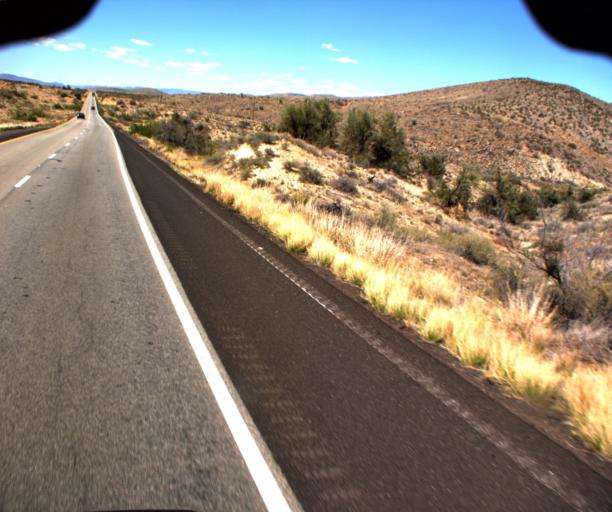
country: US
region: Arizona
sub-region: Mohave County
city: Kingman
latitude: 34.9673
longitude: -113.6701
